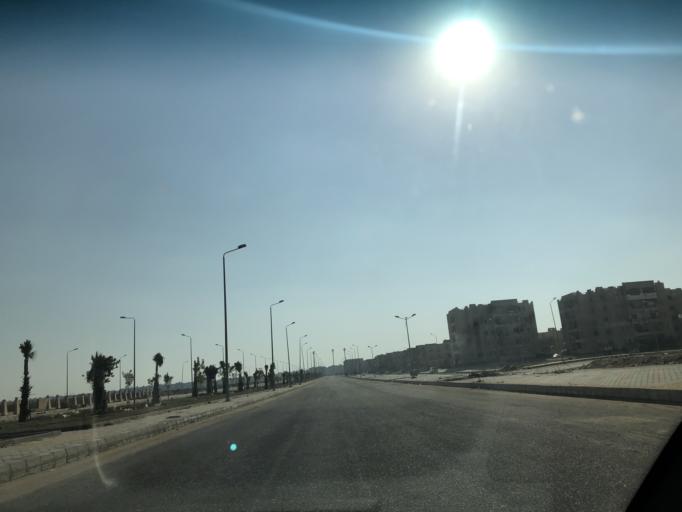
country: EG
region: Al Jizah
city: Madinat Sittah Uktubar
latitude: 29.9264
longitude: 31.0677
